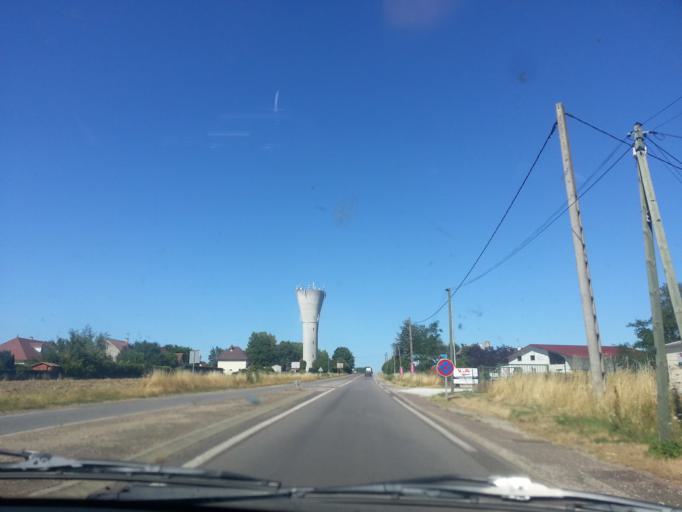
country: FR
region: Bourgogne
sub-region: Departement de Saone-et-Loire
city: Saint-Marcel
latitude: 46.7890
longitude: 4.9167
